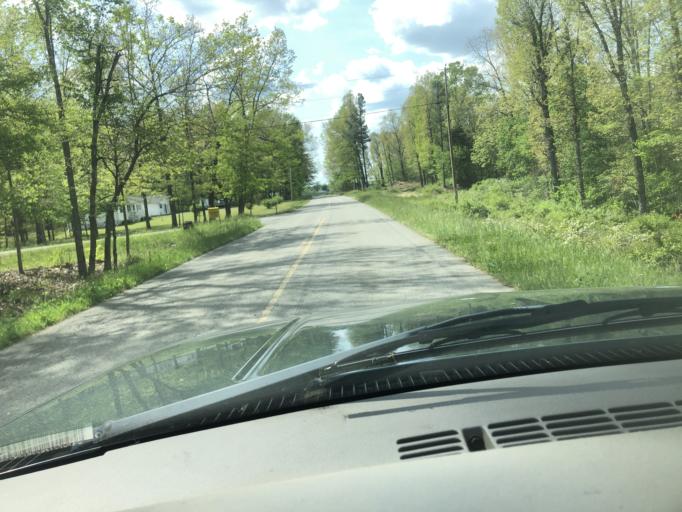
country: US
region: Tennessee
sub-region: Fentress County
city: Grimsley
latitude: 36.3137
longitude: -84.8558
